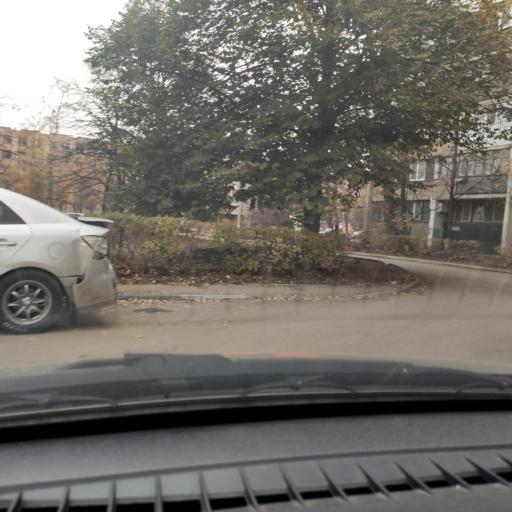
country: RU
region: Samara
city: Tol'yatti
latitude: 53.5347
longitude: 49.3093
